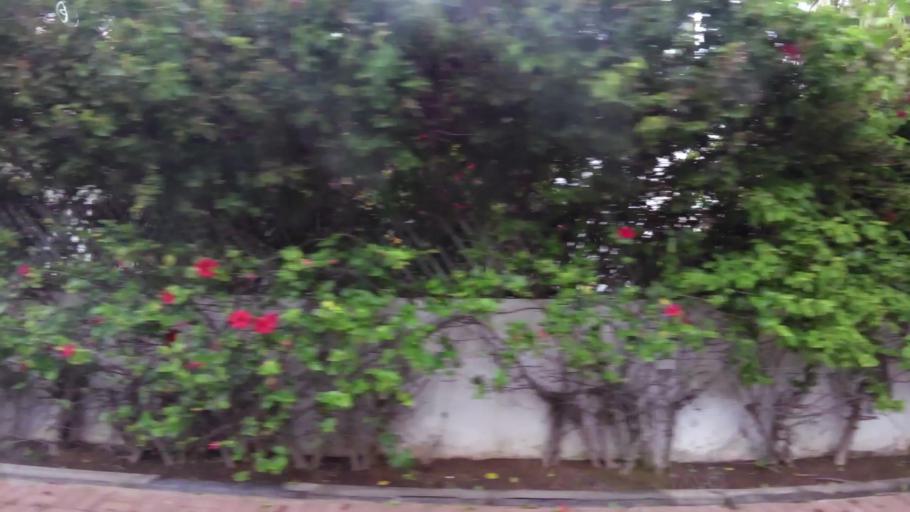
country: MA
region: Grand Casablanca
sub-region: Casablanca
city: Casablanca
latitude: 33.5997
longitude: -7.6619
